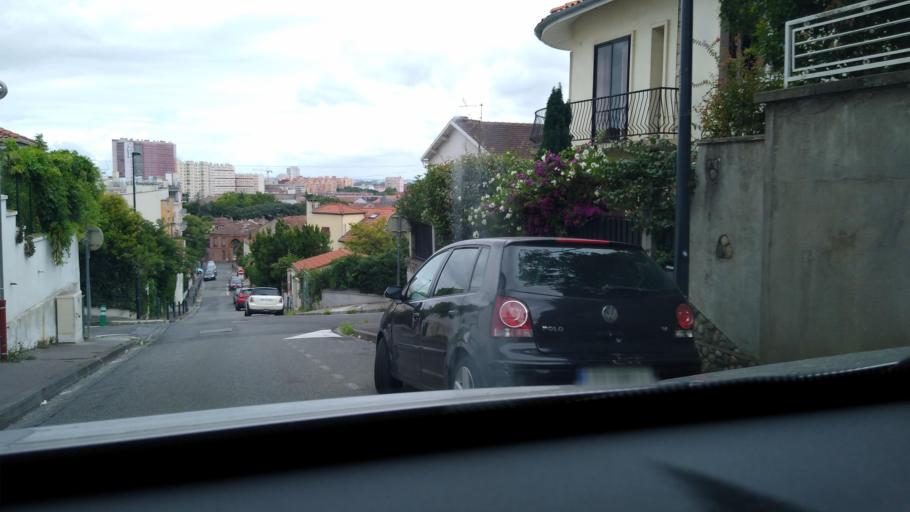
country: FR
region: Midi-Pyrenees
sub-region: Departement de la Haute-Garonne
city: Toulouse
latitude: 43.6162
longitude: 1.4591
